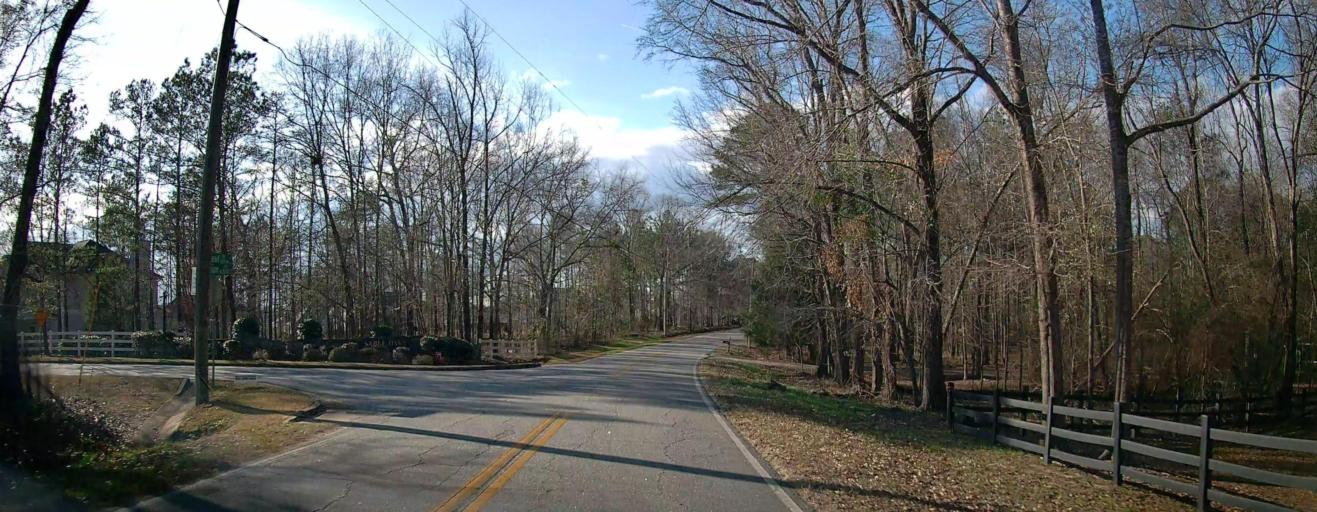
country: US
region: Georgia
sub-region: Harris County
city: Hamilton
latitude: 32.5664
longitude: -84.8004
